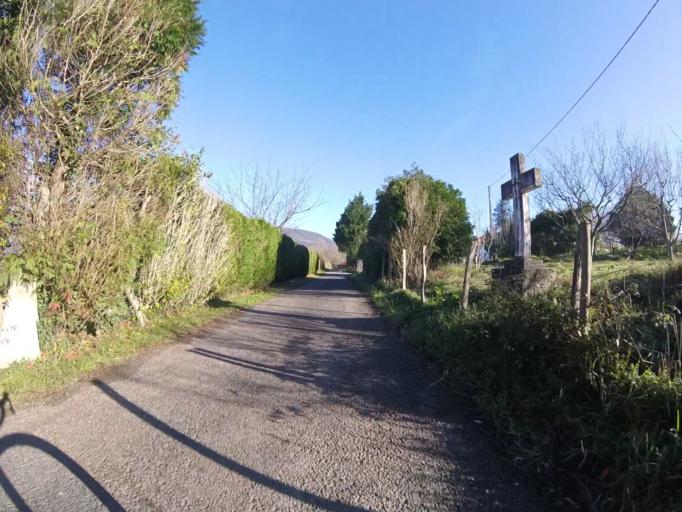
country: ES
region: Basque Country
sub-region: Provincia de Guipuzcoa
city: Usurbil
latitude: 43.2731
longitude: -2.0703
